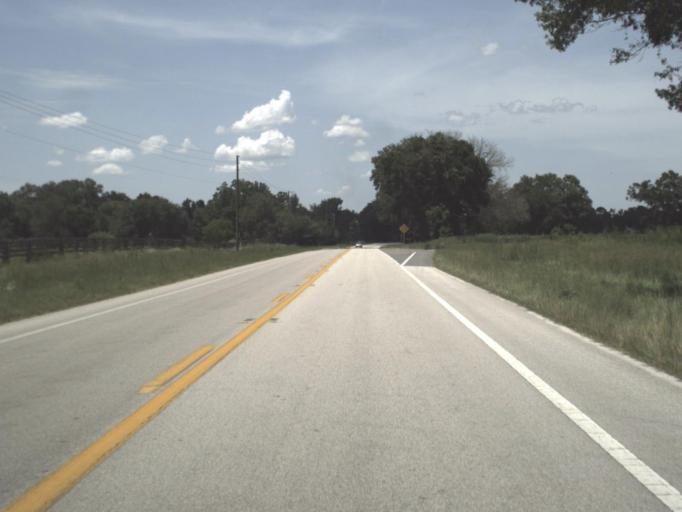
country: US
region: Florida
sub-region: Gilchrist County
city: Trenton
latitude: 29.5929
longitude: -82.8232
